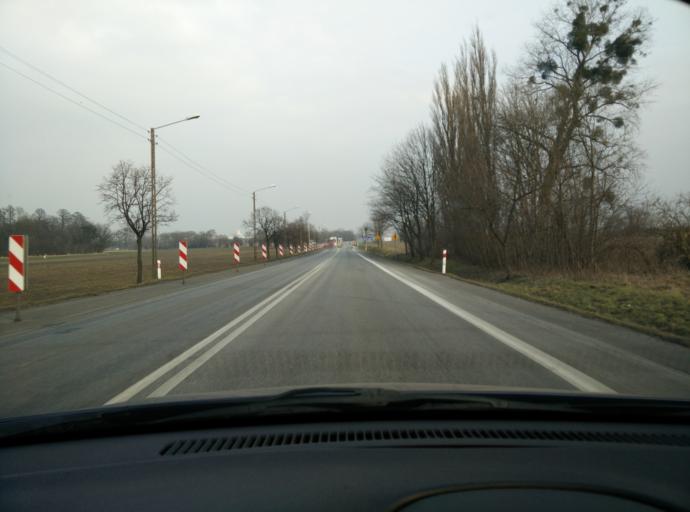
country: PL
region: Greater Poland Voivodeship
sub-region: Powiat sredzki
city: Sroda Wielkopolska
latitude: 52.2282
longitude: 17.2290
